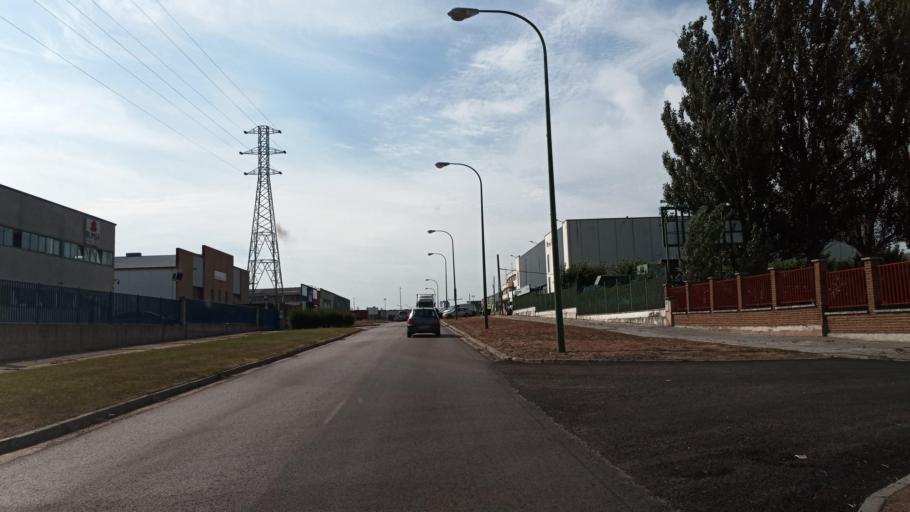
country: ES
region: Castille and Leon
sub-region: Provincia de Burgos
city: Burgos
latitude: 42.3631
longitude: -3.6431
